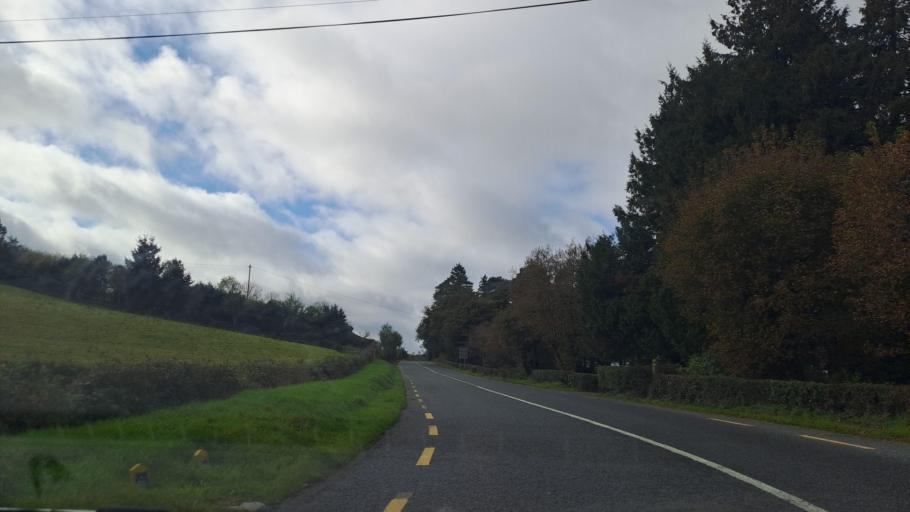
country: IE
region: Ulster
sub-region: An Cabhan
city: Bailieborough
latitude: 53.9326
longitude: -6.9192
